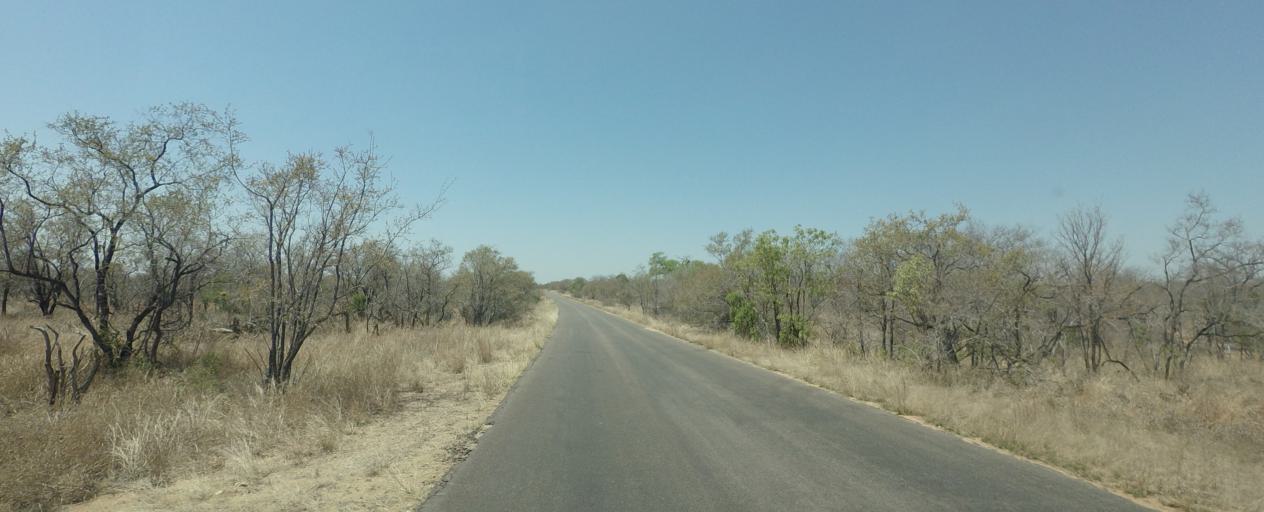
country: ZA
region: Limpopo
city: Thulamahashi
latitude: -24.4724
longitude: 31.4269
